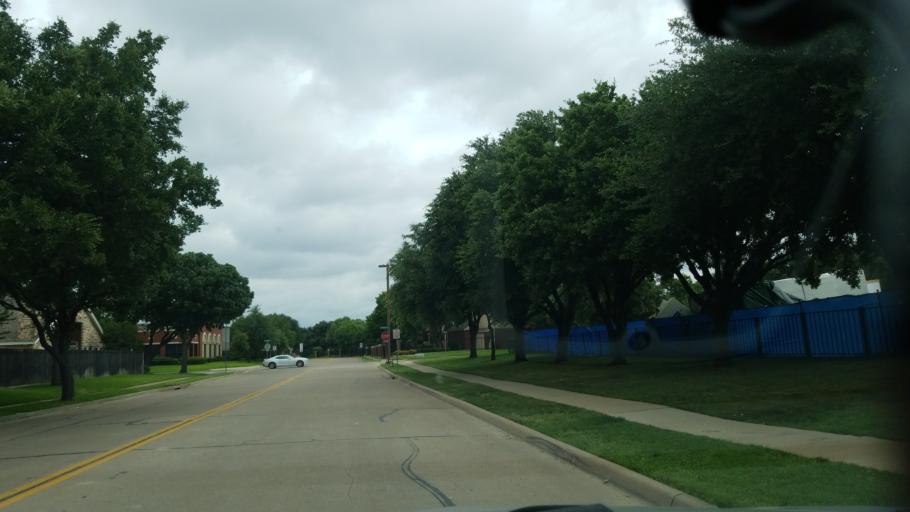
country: US
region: Texas
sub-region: Dallas County
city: Farmers Branch
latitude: 32.9322
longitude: -96.9489
